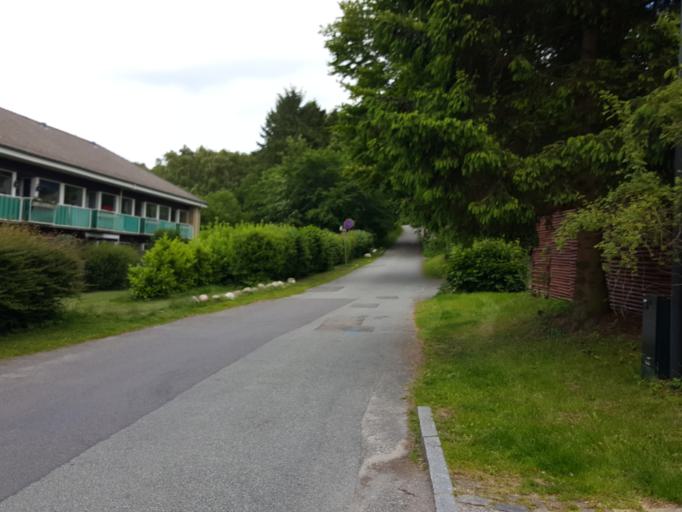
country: DK
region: Capital Region
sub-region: Rudersdal Kommune
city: Birkerod
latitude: 55.8456
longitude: 12.4393
